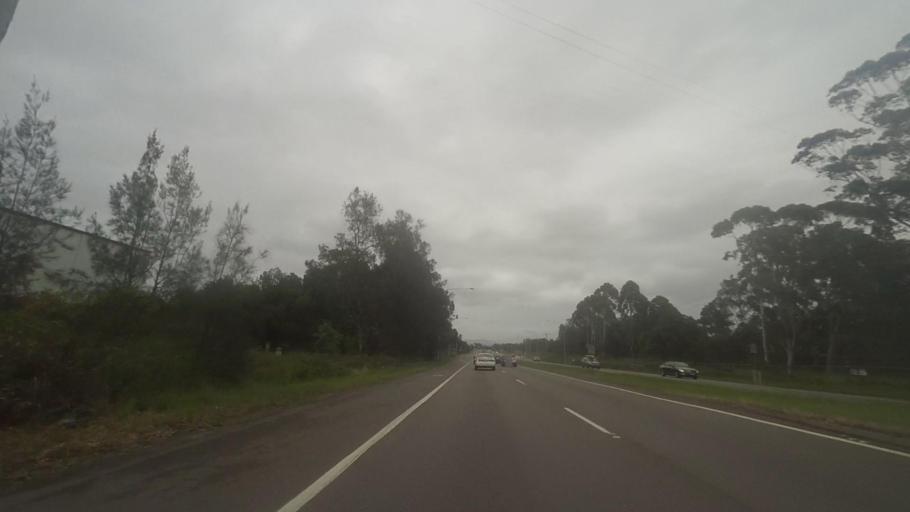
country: AU
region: New South Wales
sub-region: Newcastle
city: Beresfield
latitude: -32.8154
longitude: 151.6988
